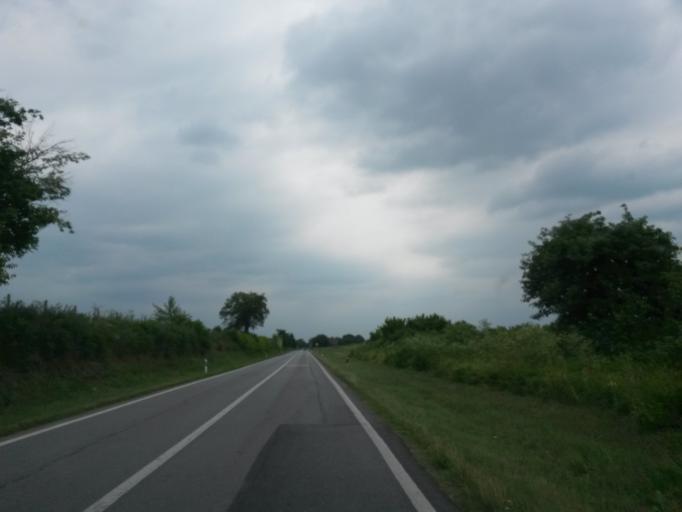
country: HR
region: Vukovarsko-Srijemska
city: Negoslavci
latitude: 45.3072
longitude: 19.0811
